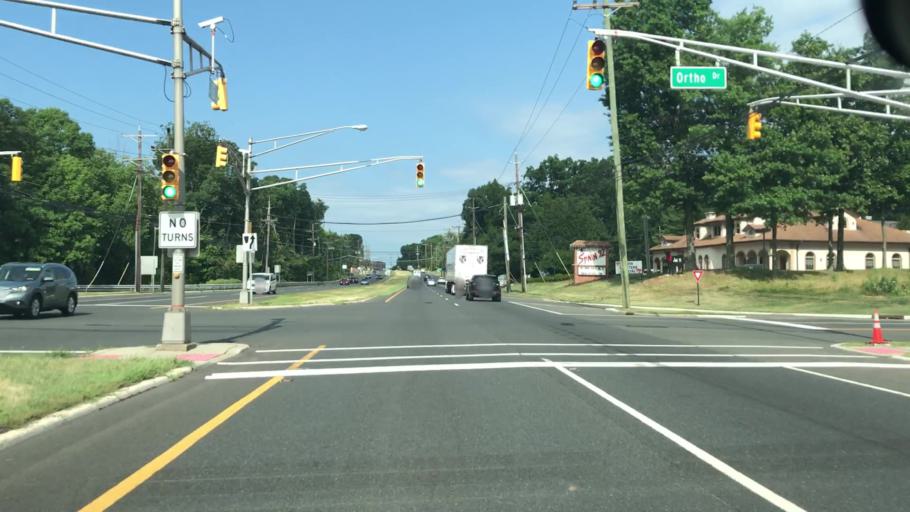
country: US
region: New Jersey
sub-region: Somerset County
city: Bradley Gardens
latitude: 40.5746
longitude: -74.6543
